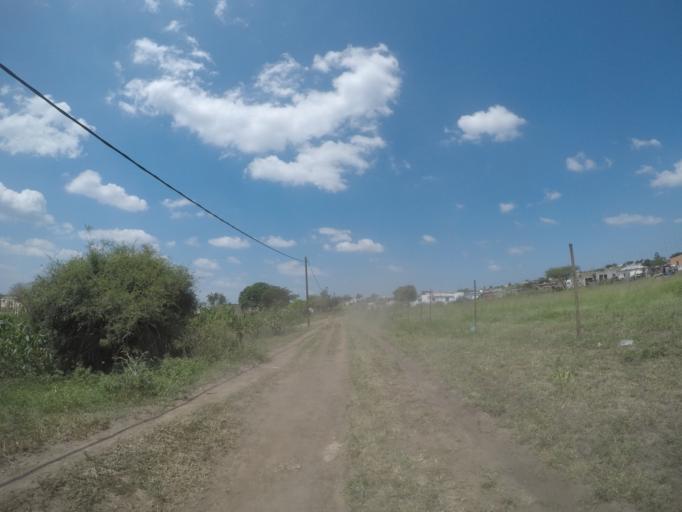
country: ZA
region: KwaZulu-Natal
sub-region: uThungulu District Municipality
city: Empangeni
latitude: -28.5900
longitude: 31.7382
